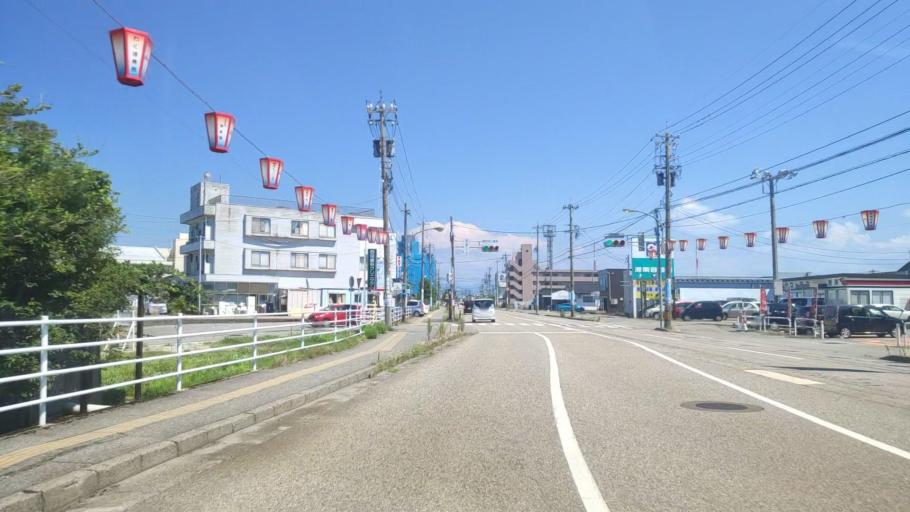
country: JP
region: Ishikawa
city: Kanazawa-shi
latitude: 36.6008
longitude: 136.5945
